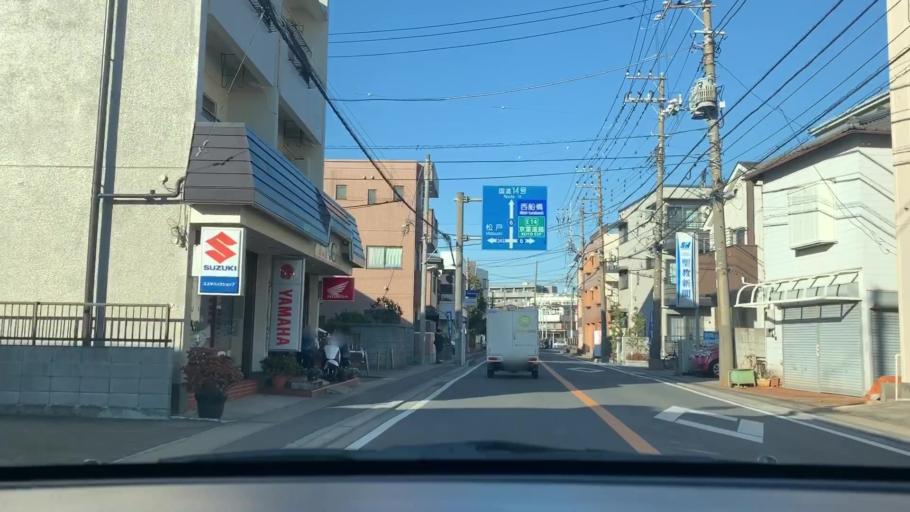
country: JP
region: Tokyo
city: Urayasu
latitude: 35.7125
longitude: 139.9194
